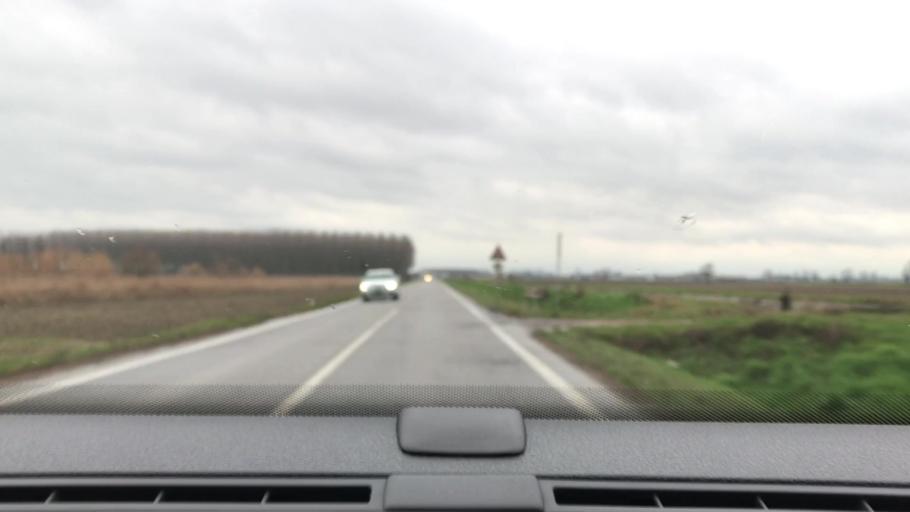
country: IT
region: Lombardy
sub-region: Provincia di Cremona
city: Torricella del Pizzo
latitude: 45.0231
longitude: 10.3126
